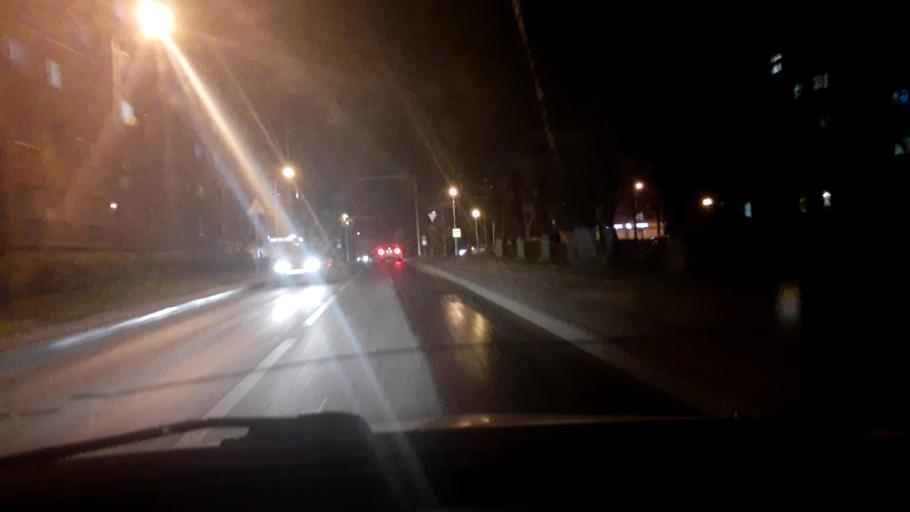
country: RU
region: Bashkortostan
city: Ufa
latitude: 54.7899
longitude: 56.0307
